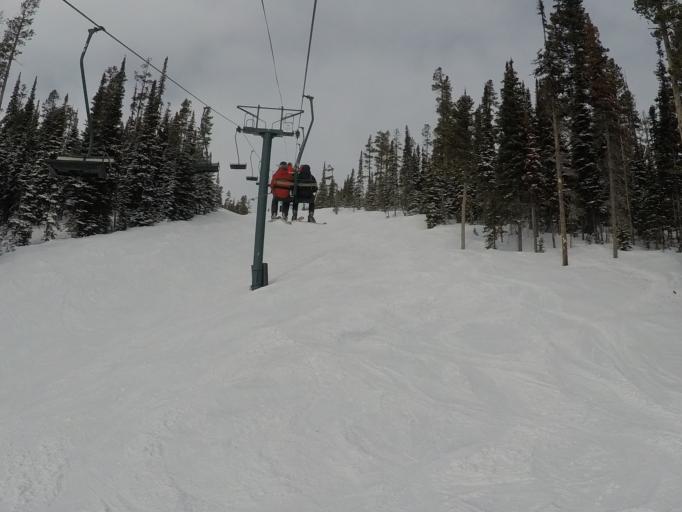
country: US
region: Montana
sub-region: Meagher County
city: White Sulphur Springs
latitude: 46.8394
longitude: -110.7070
